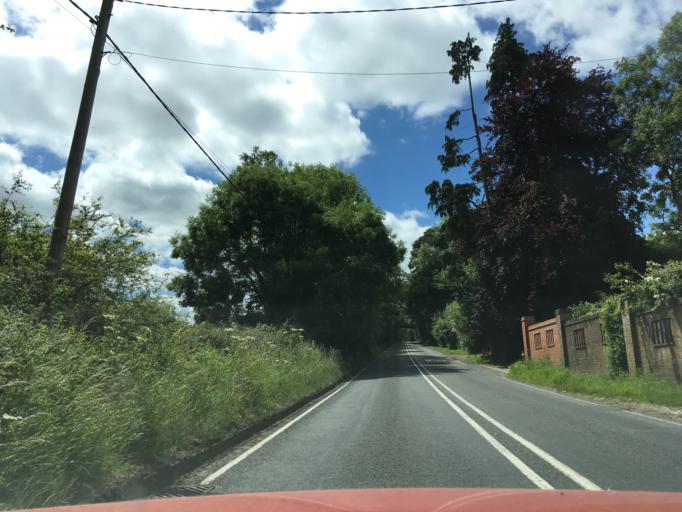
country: GB
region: England
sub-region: Hampshire
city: Highclere
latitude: 51.3479
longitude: -1.3704
